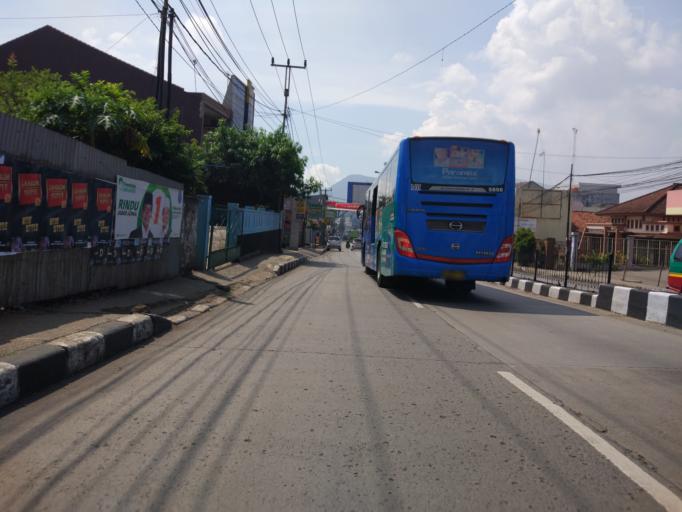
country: ID
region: West Java
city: Cileunyi
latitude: -6.9372
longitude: 107.7597
